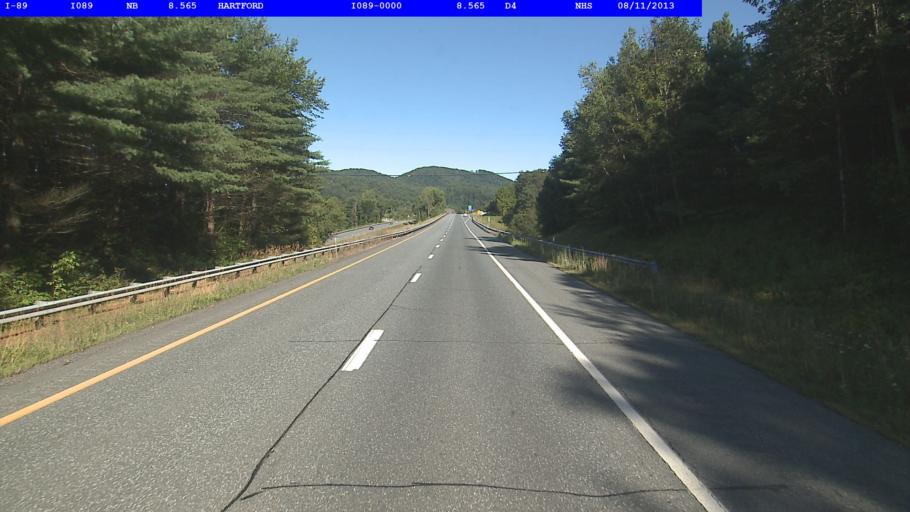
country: US
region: Vermont
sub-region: Windsor County
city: Wilder
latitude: 43.7247
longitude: -72.4218
